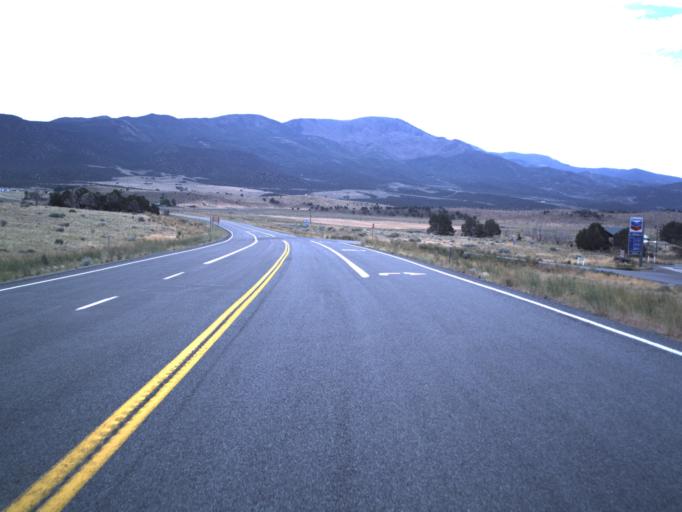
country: US
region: Utah
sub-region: Beaver County
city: Beaver
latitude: 38.6143
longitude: -112.6054
